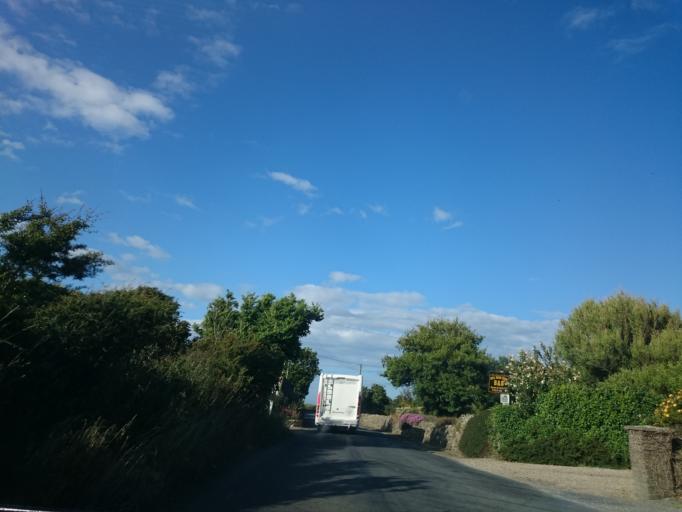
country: IE
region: Leinster
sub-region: Loch Garman
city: Loch Garman
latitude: 52.1866
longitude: -6.5687
